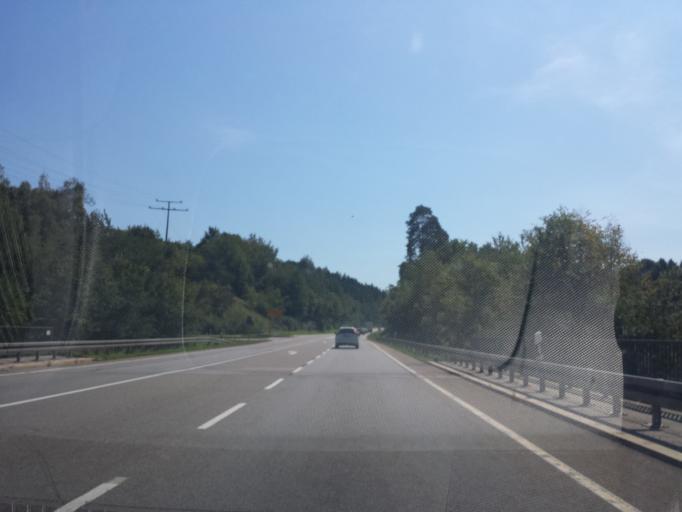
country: DE
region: Bavaria
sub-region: Lower Bavaria
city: Stallwang
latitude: 49.0612
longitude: 12.6425
